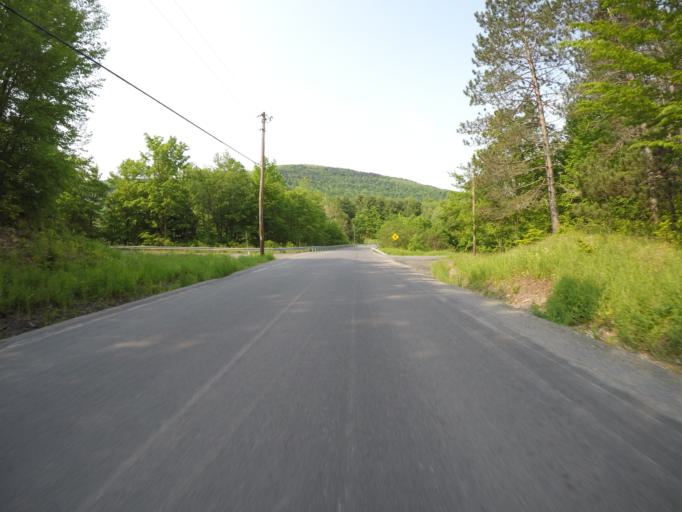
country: US
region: New York
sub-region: Sullivan County
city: Livingston Manor
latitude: 42.1111
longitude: -74.7342
